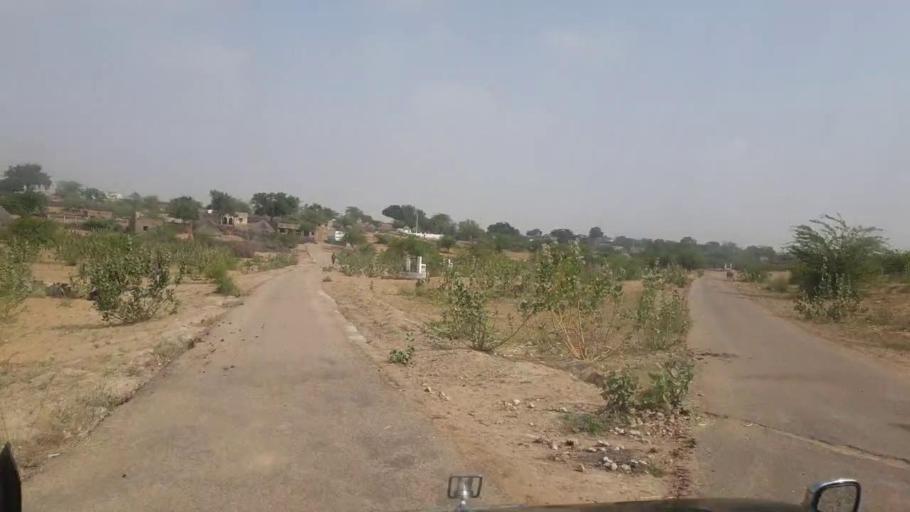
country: PK
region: Sindh
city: Islamkot
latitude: 25.1318
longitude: 70.1443
